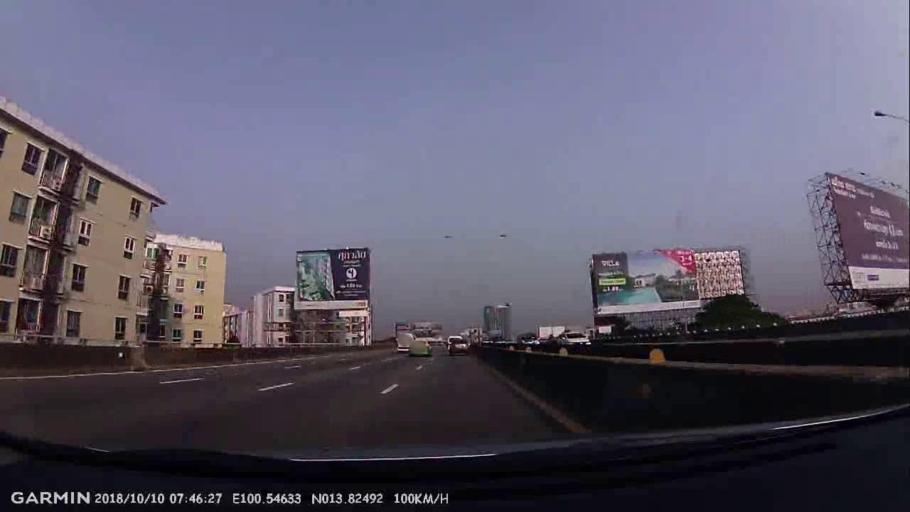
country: TH
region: Bangkok
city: Chatuchak
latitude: 13.8249
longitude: 100.5464
